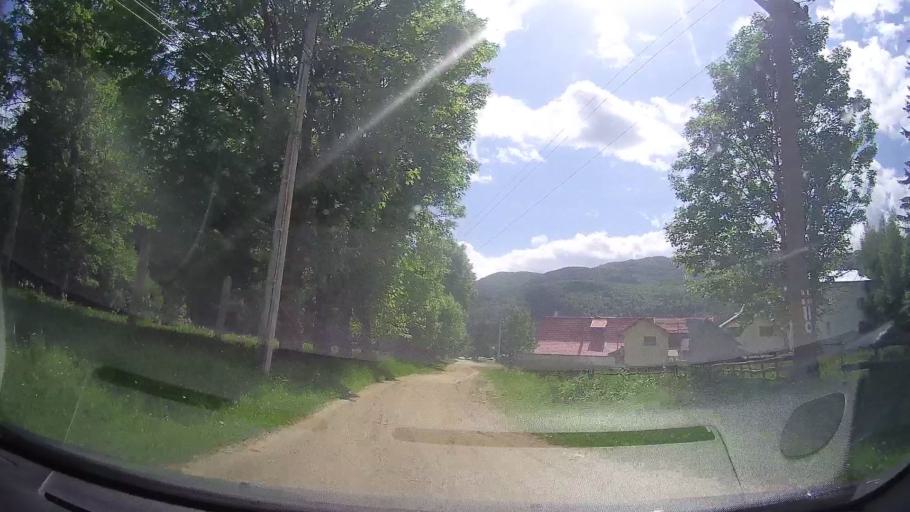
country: RO
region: Brasov
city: Crivina
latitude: 45.4571
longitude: 25.9416
